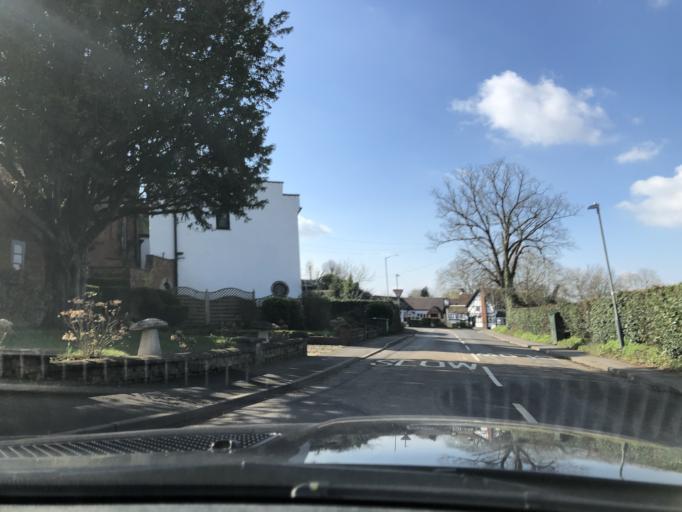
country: GB
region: England
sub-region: Warwickshire
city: Royal Leamington Spa
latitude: 52.2783
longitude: -1.4955
